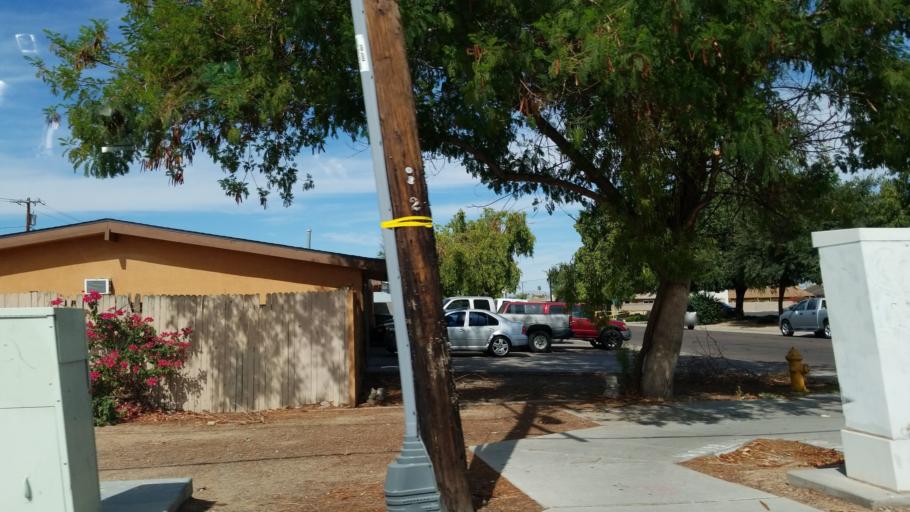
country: US
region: Arizona
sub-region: Maricopa County
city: Glendale
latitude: 33.4915
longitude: -112.1866
